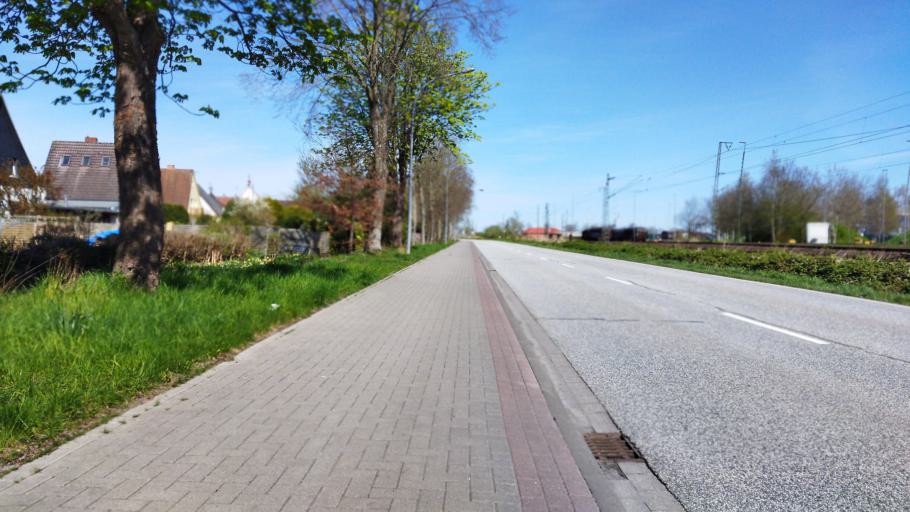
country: DE
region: Lower Saxony
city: Brake (Unterweser)
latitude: 53.3407
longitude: 8.4805
